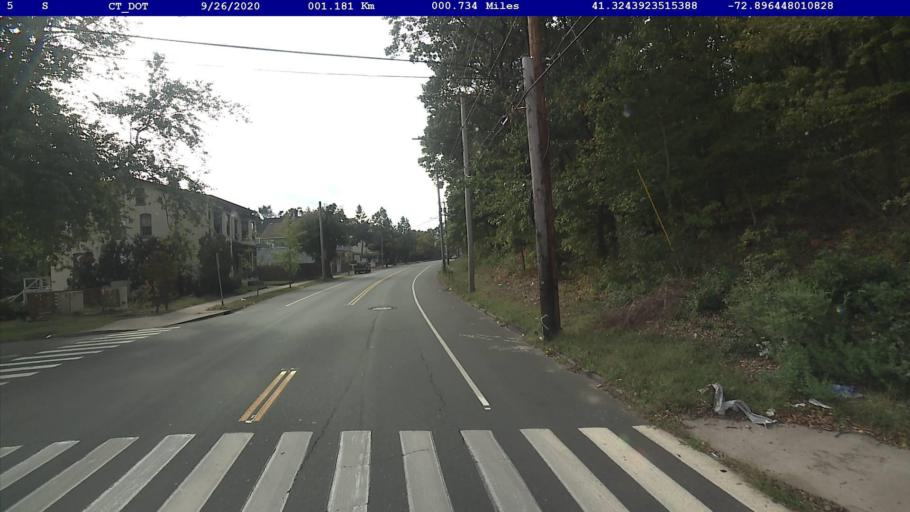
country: US
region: Connecticut
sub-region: New Haven County
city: New Haven
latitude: 41.3244
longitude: -72.8965
